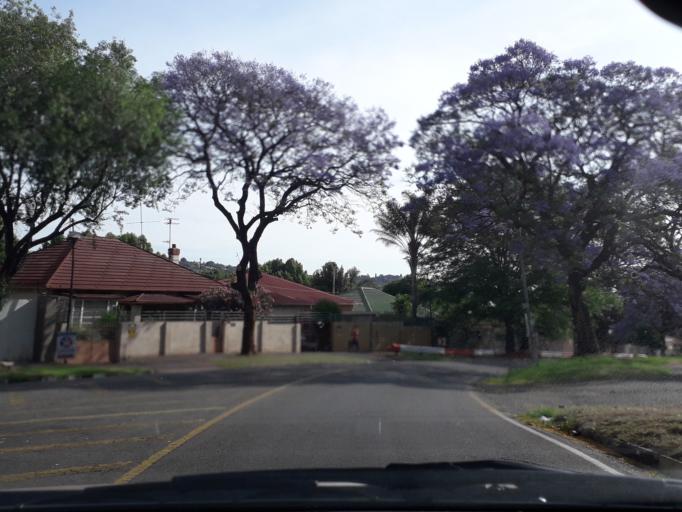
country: ZA
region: Gauteng
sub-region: City of Johannesburg Metropolitan Municipality
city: Johannesburg
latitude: -26.1848
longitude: 28.0834
